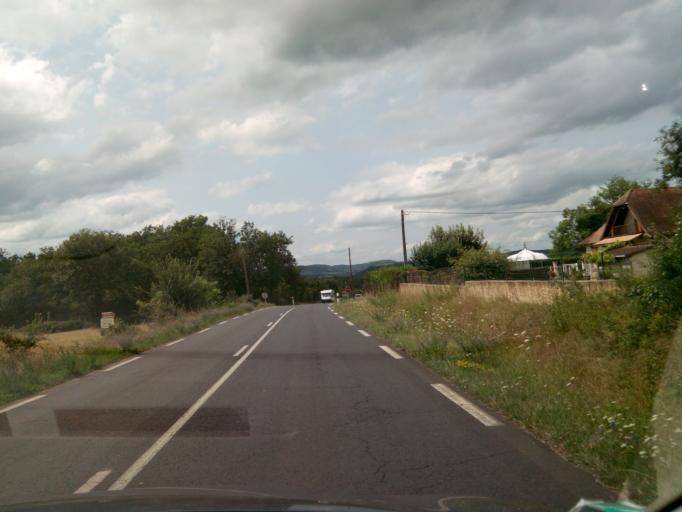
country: FR
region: Midi-Pyrenees
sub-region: Departement du Lot
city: Vayrac
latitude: 44.9870
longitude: 1.6699
